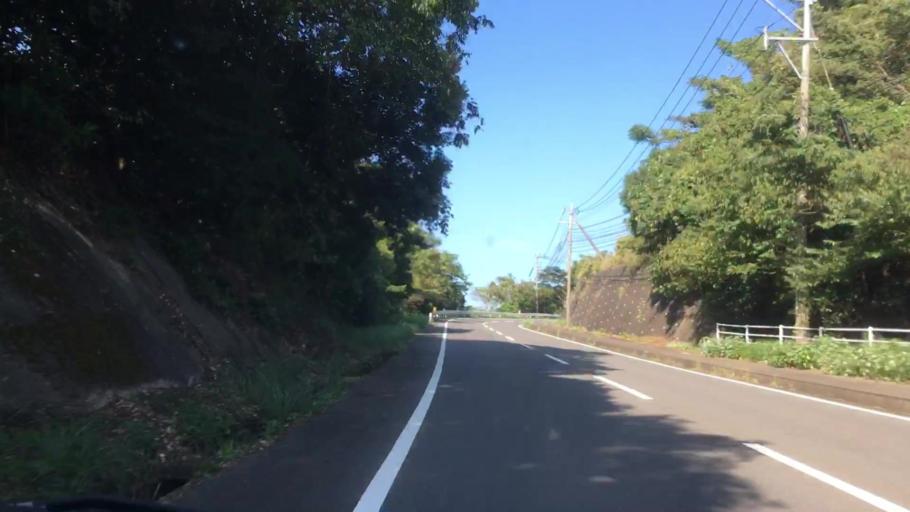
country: JP
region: Nagasaki
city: Sasebo
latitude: 33.0042
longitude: 129.6591
